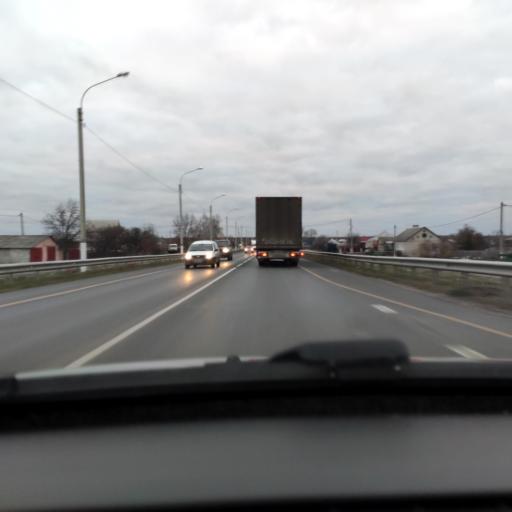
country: RU
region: Lipetsk
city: Khlevnoye
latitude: 52.2563
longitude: 39.1517
